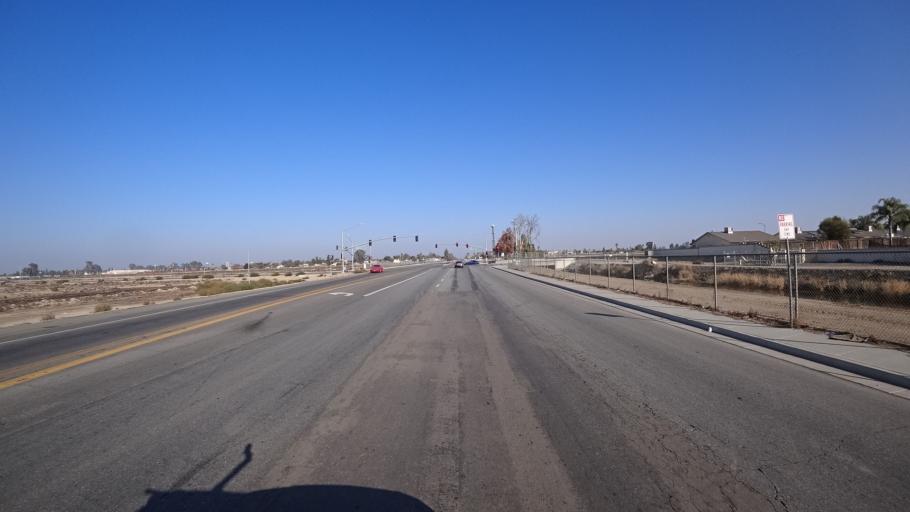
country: US
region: California
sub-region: Kern County
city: Greenfield
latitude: 35.2877
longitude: -119.0212
